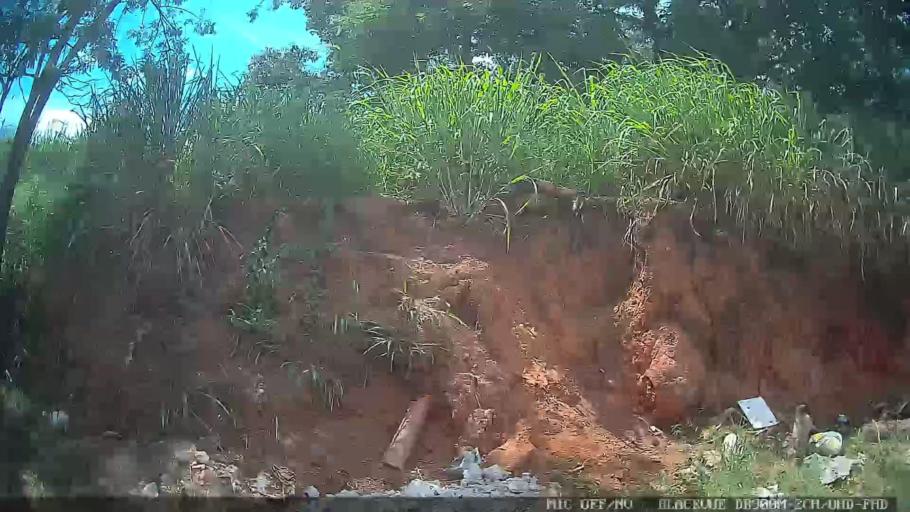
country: BR
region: Sao Paulo
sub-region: Braganca Paulista
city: Braganca Paulista
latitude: -23.0300
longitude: -46.5397
